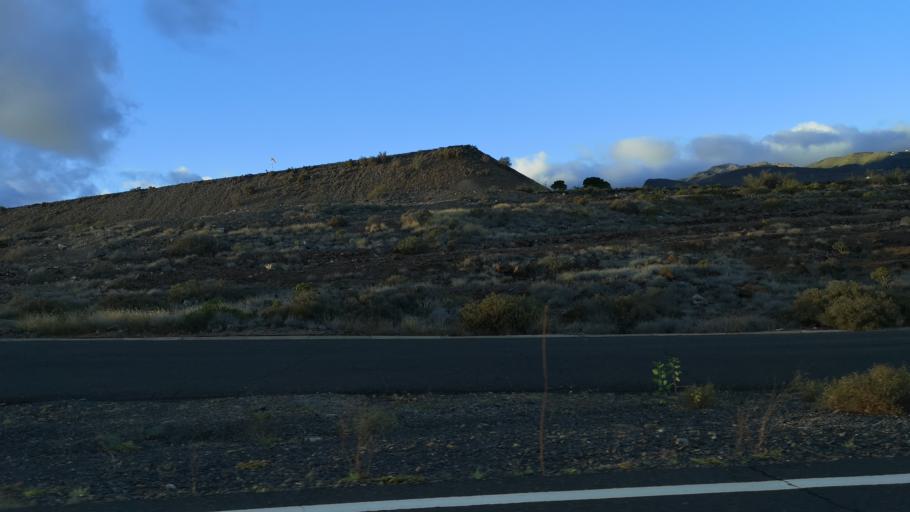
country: ES
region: Canary Islands
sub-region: Provincia de Santa Cruz de Tenerife
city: Alajero
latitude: 28.0277
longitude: -17.2054
